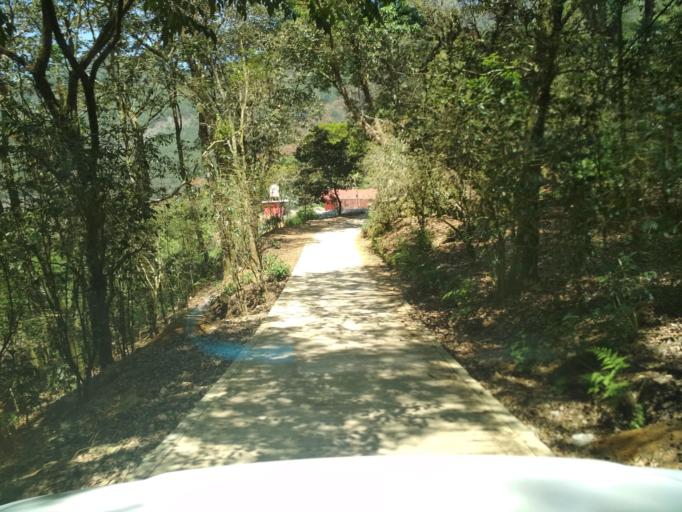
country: MX
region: Veracruz
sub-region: Tlilapan
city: Tonalixco
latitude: 18.7790
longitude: -97.0763
